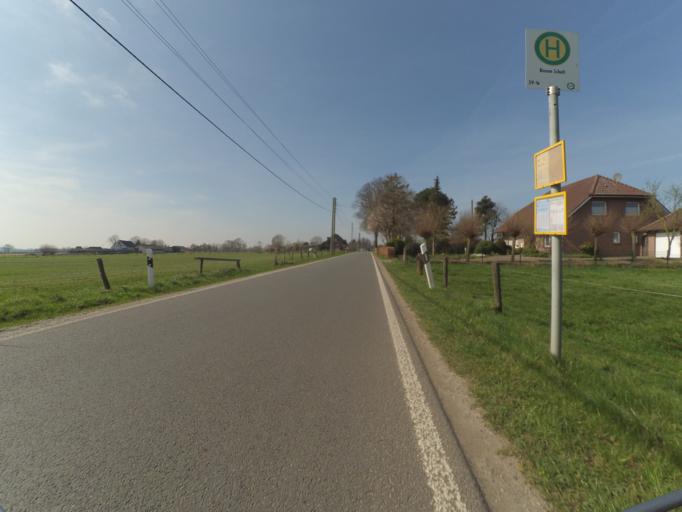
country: DE
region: North Rhine-Westphalia
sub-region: Regierungsbezirk Dusseldorf
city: Kranenburg
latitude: 51.8094
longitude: 6.0637
